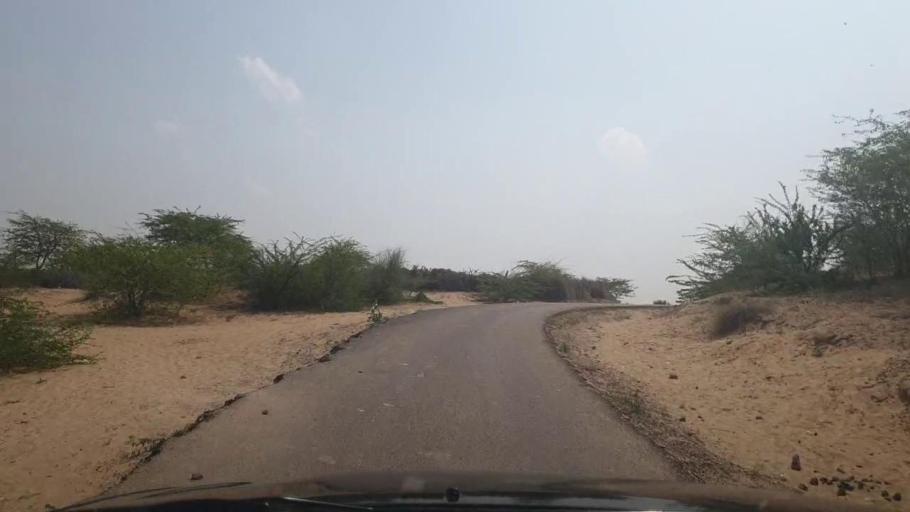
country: PK
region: Sindh
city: Islamkot
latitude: 25.0042
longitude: 70.4161
